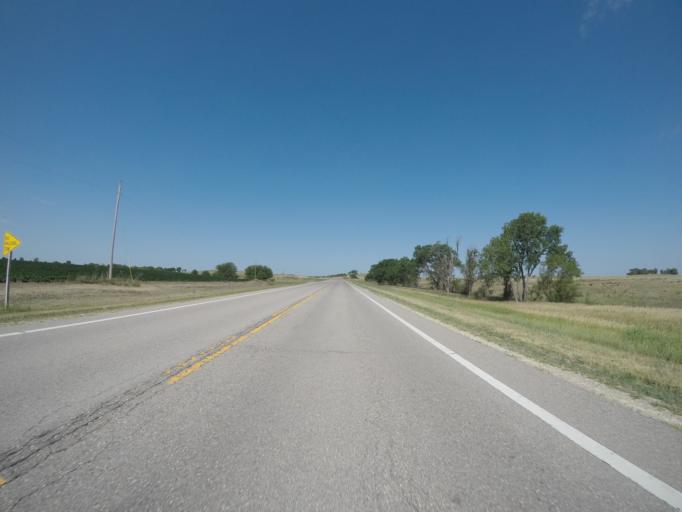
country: US
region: Kansas
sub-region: Clay County
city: Clay Center
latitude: 39.3783
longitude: -97.3814
